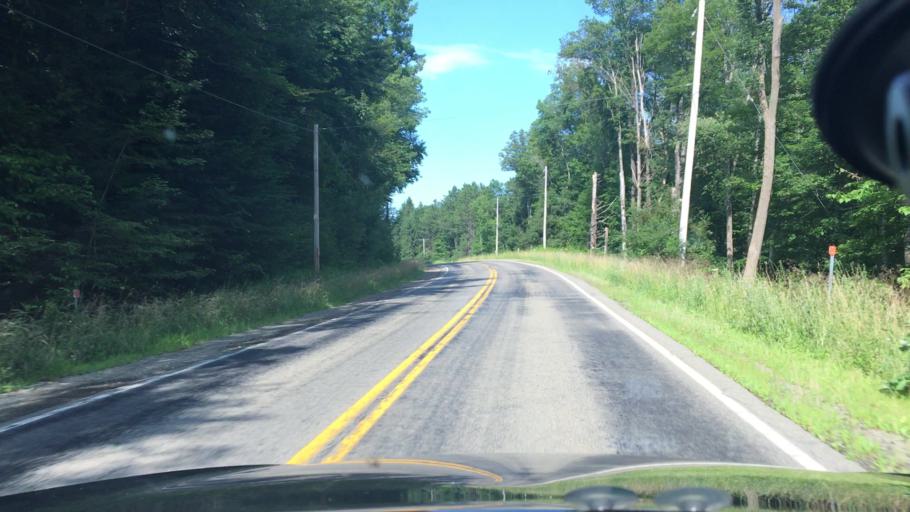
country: US
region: New York
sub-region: Chautauqua County
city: Lakewood
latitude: 42.2555
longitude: -79.3518
